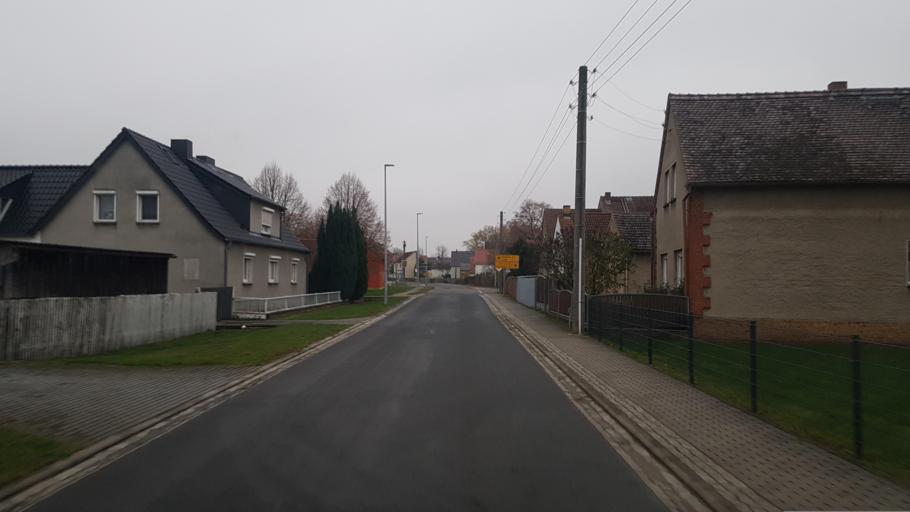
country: DE
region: Brandenburg
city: Hermsdorf
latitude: 51.4061
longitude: 13.8935
